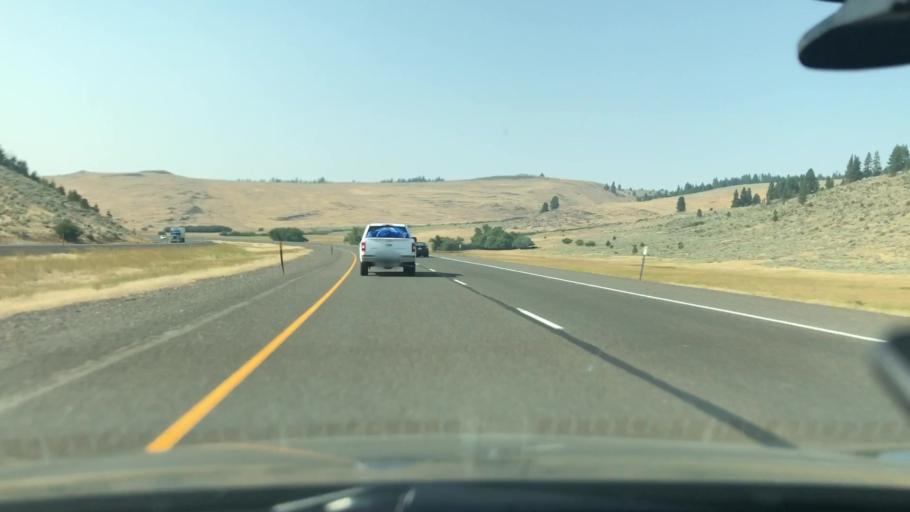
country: US
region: Oregon
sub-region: Union County
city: Union
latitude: 45.1653
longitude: -117.9644
